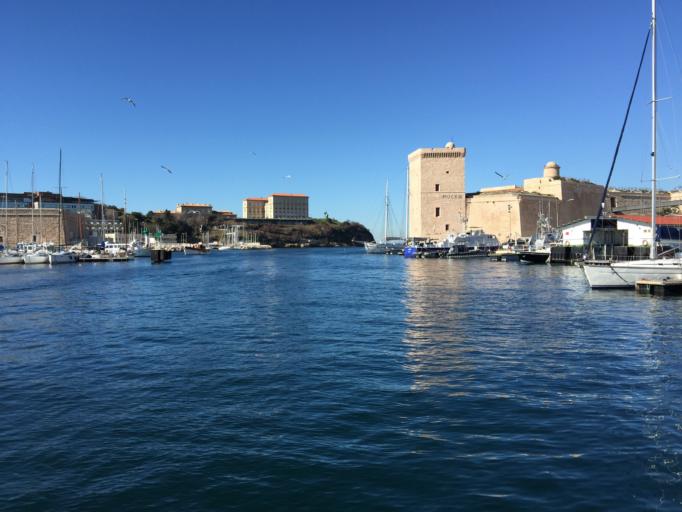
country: FR
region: Provence-Alpes-Cote d'Azur
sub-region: Departement des Bouches-du-Rhone
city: Marseille 02
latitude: 43.2943
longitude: 5.3651
